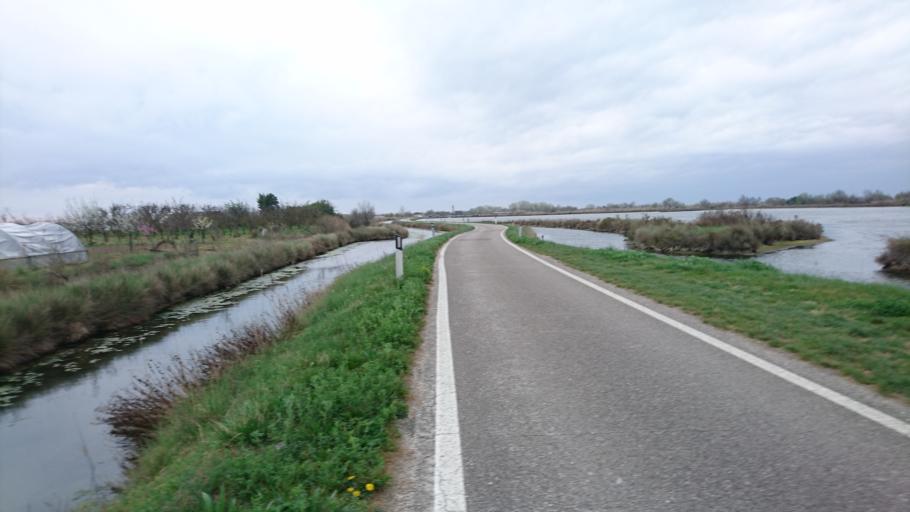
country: IT
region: Veneto
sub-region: Provincia di Venezia
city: Cavallino
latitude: 45.4915
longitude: 12.5059
